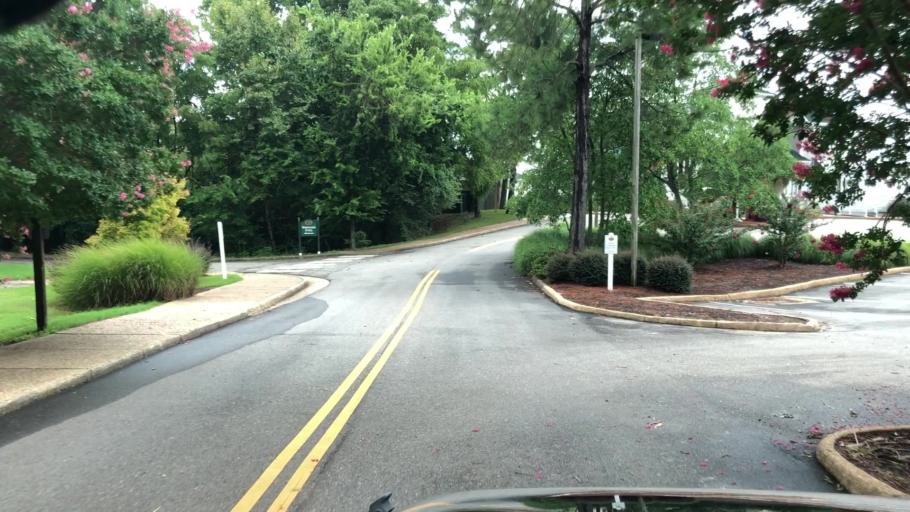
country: US
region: Virginia
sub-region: City of Williamsburg
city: Williamsburg
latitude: 37.2237
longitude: -76.6635
